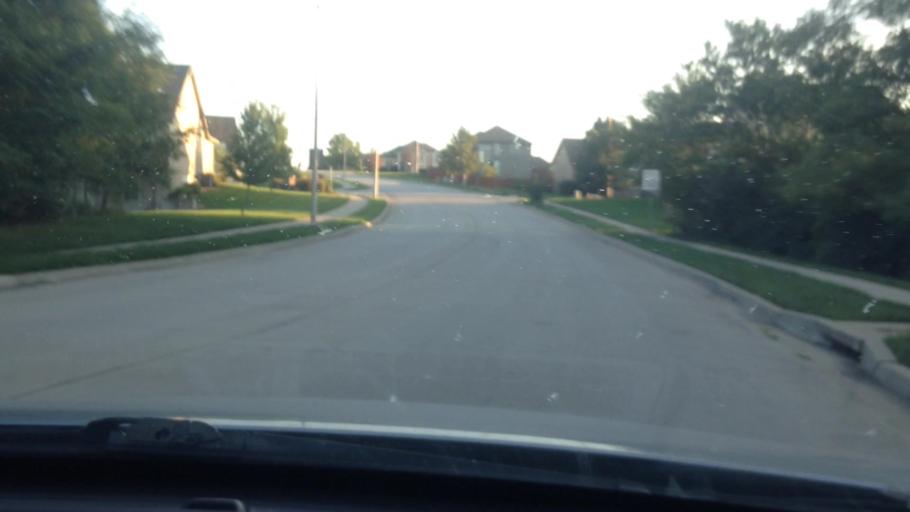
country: US
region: Missouri
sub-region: Clay County
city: Smithville
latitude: 39.2941
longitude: -94.5893
